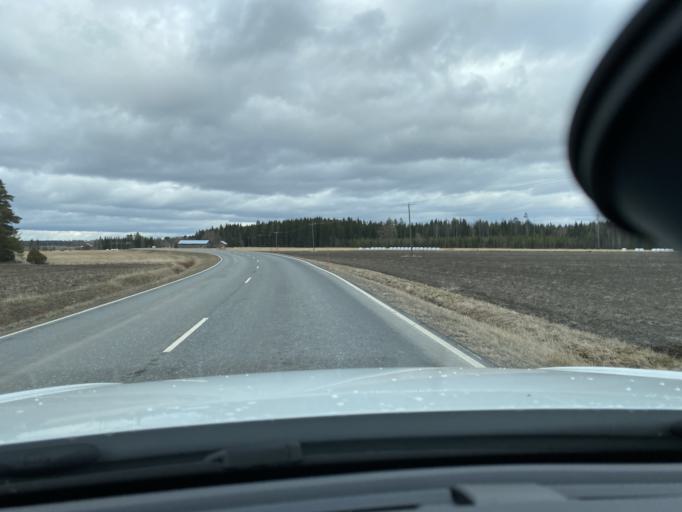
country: FI
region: Pirkanmaa
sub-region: Lounais-Pirkanmaa
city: Punkalaidun
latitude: 61.1034
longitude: 23.1706
